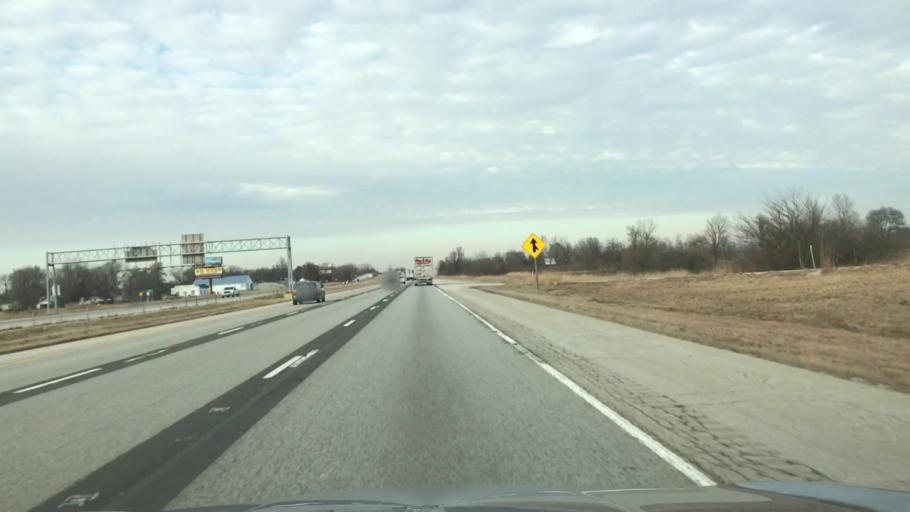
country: US
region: Illinois
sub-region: Sangamon County
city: Divernon
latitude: 39.6187
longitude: -89.6468
